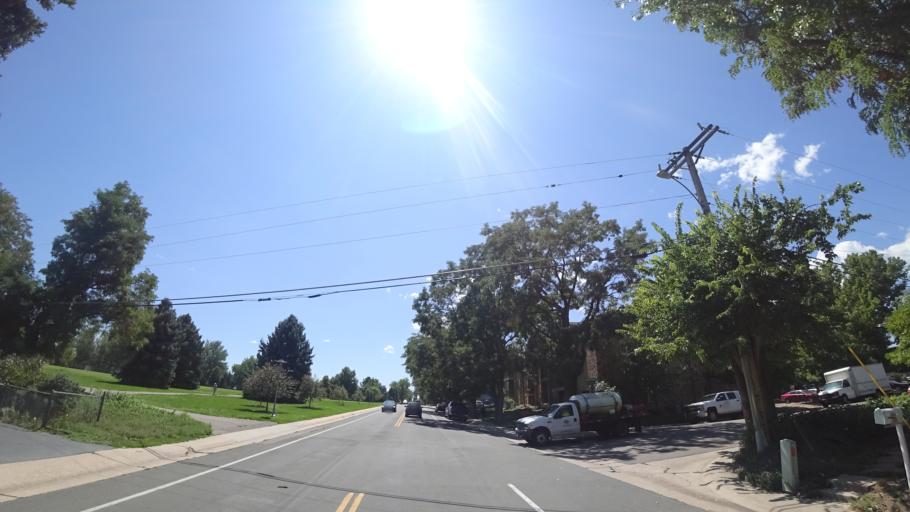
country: US
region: Colorado
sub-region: Arapahoe County
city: Littleton
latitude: 39.6098
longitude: -105.0021
